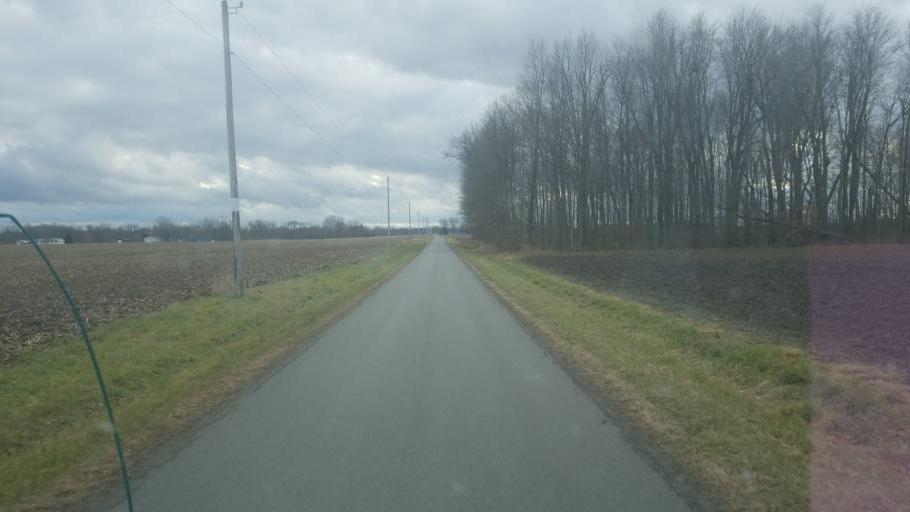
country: US
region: Ohio
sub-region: Wyandot County
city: Upper Sandusky
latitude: 40.7791
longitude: -83.1499
